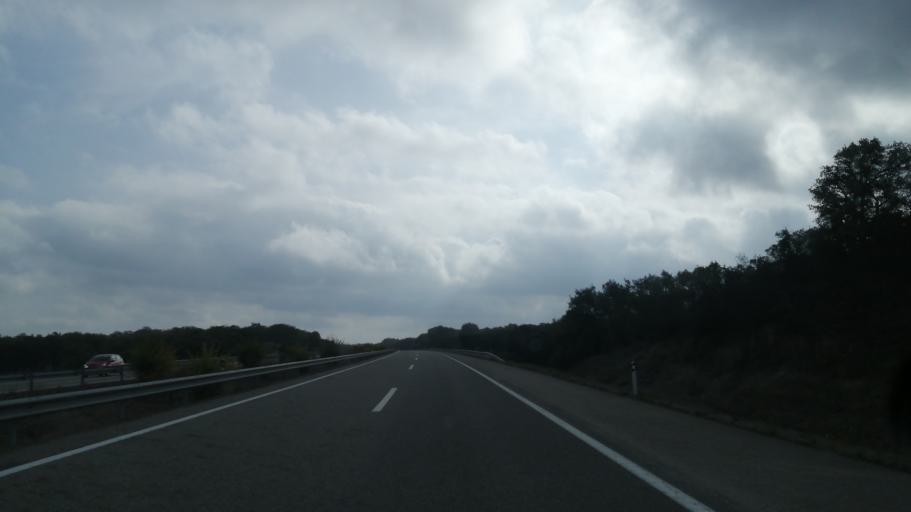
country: PT
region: Evora
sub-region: Vendas Novas
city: Vendas Novas
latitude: 38.6378
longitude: -8.3395
